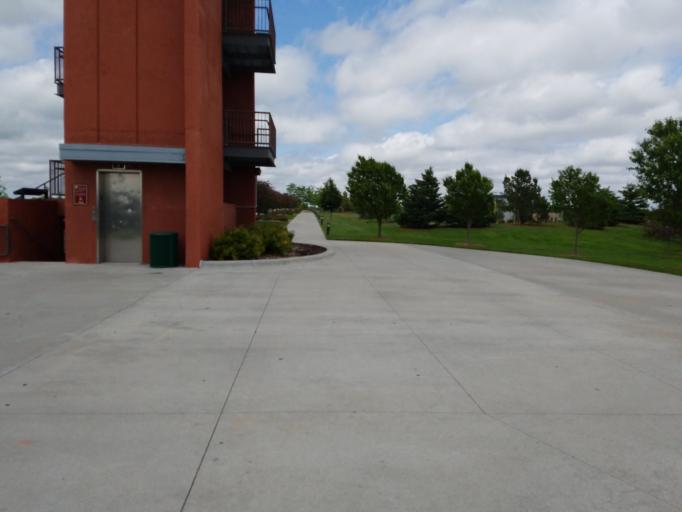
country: US
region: Nebraska
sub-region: Buffalo County
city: Kearney
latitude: 40.6820
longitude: -99.1074
